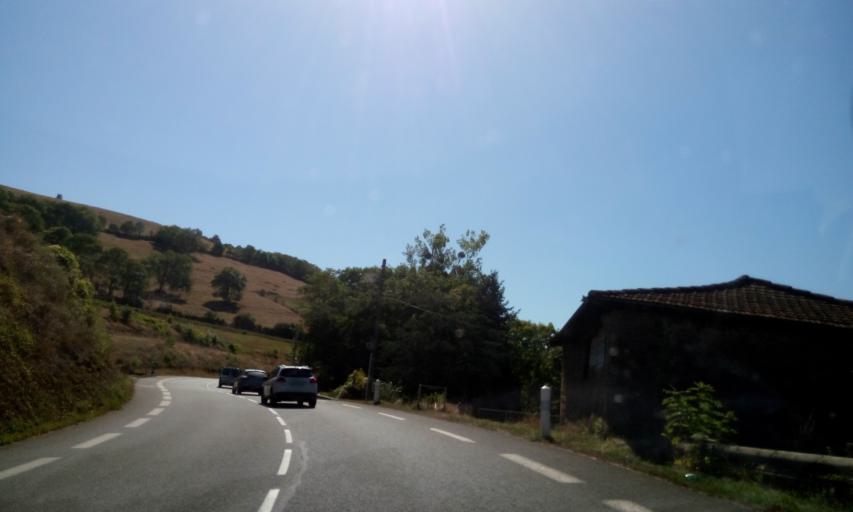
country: FR
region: Rhone-Alpes
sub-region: Departement du Rhone
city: Saint-Verand
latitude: 45.9790
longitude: 4.5067
